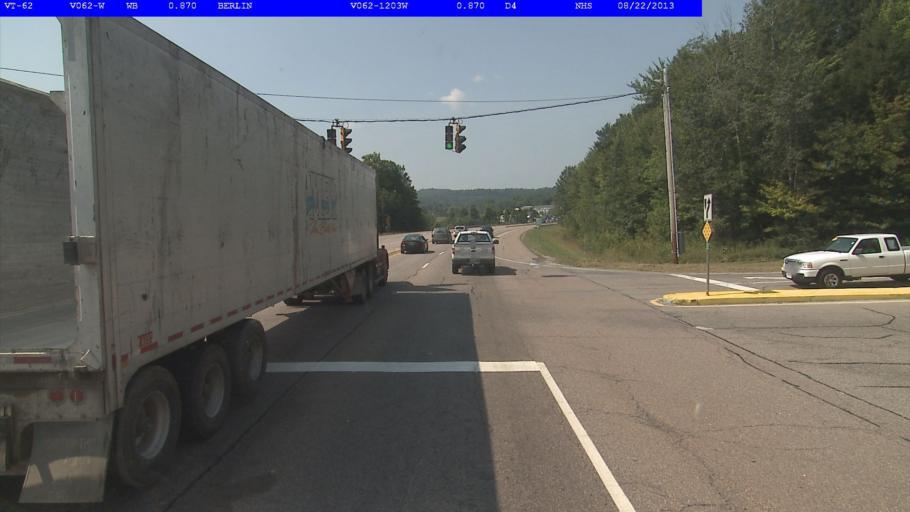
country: US
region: Vermont
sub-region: Washington County
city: Montpelier
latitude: 44.2133
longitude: -72.5676
